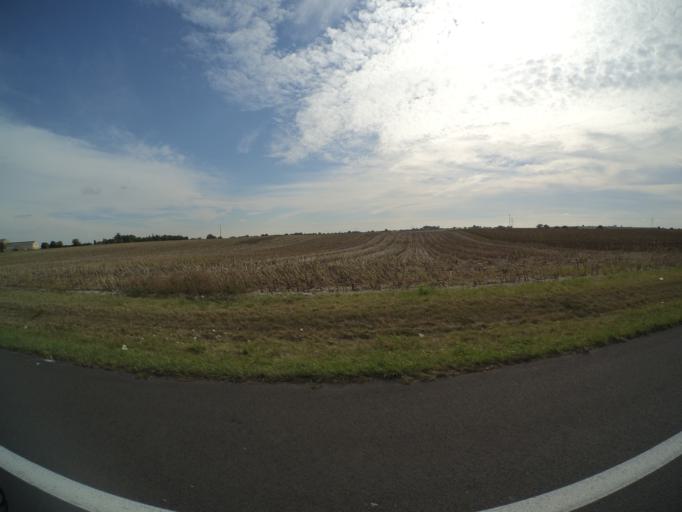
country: FR
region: Pays de la Loire
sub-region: Departement de Maine-et-Loire
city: Vaudelnay
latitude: 47.2102
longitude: -0.1858
